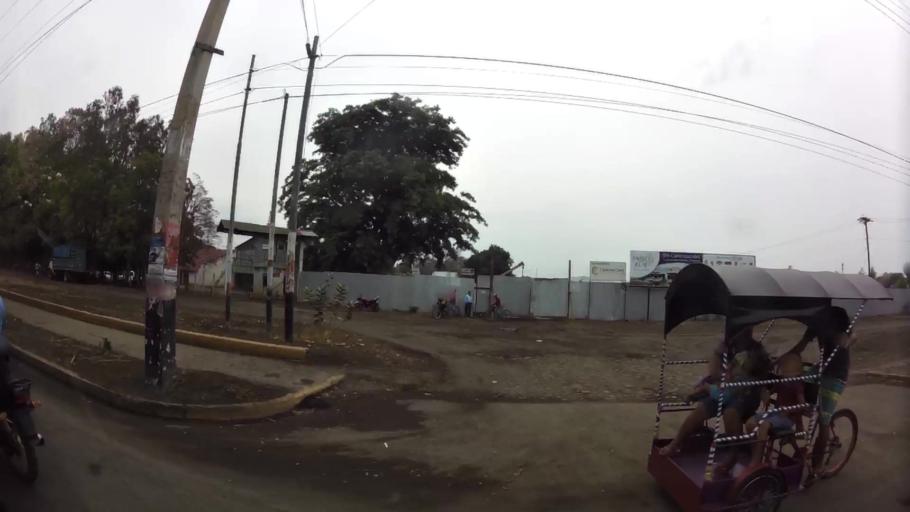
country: NI
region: Leon
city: Leon
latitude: 12.4469
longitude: -86.8720
